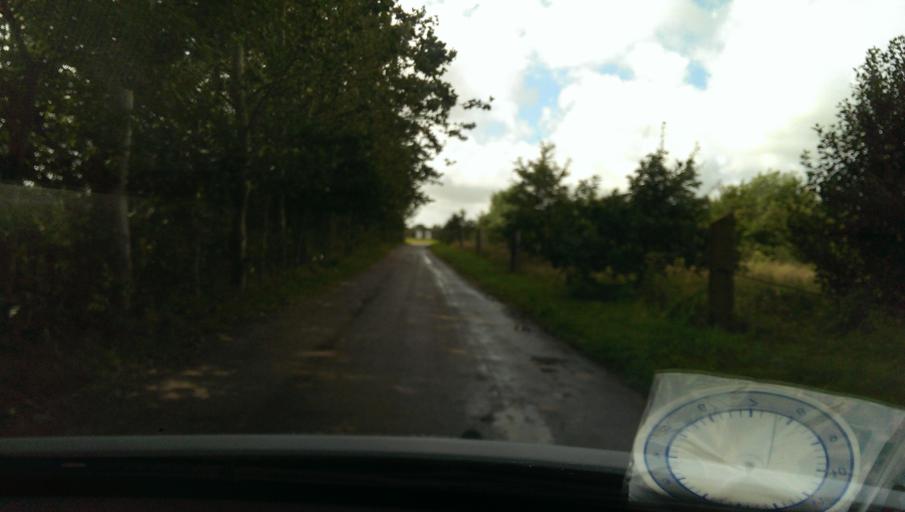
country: DK
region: South Denmark
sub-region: Varde Kommune
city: Varde
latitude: 55.6102
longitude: 8.4451
